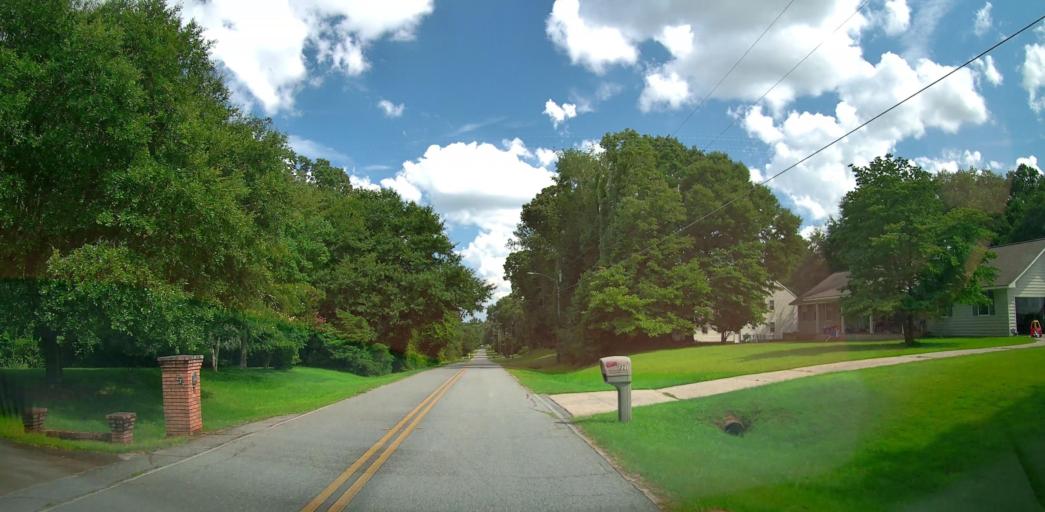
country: US
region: Georgia
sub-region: Houston County
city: Centerville
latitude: 32.5808
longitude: -83.6665
